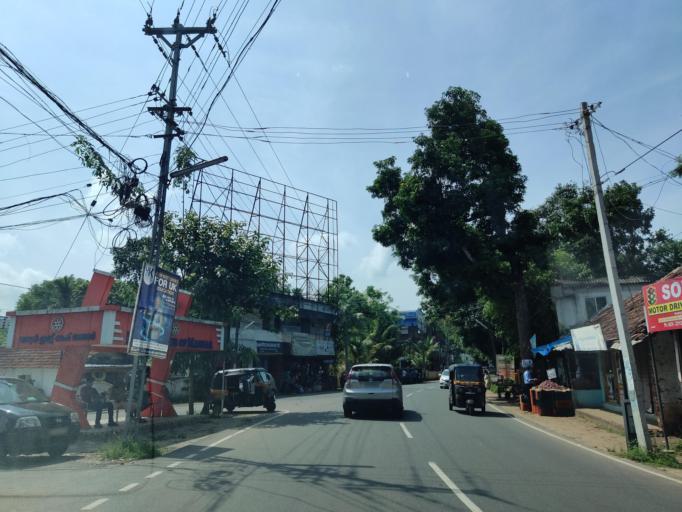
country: IN
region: Kerala
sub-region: Alappuzha
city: Mavelikara
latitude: 9.3169
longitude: 76.5338
